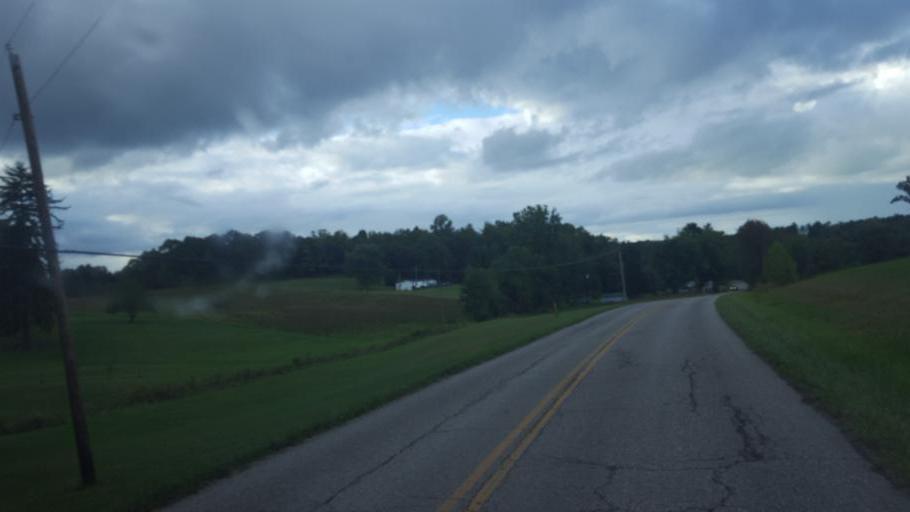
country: US
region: Ohio
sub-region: Jackson County
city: Oak Hill
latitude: 38.9059
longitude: -82.5838
